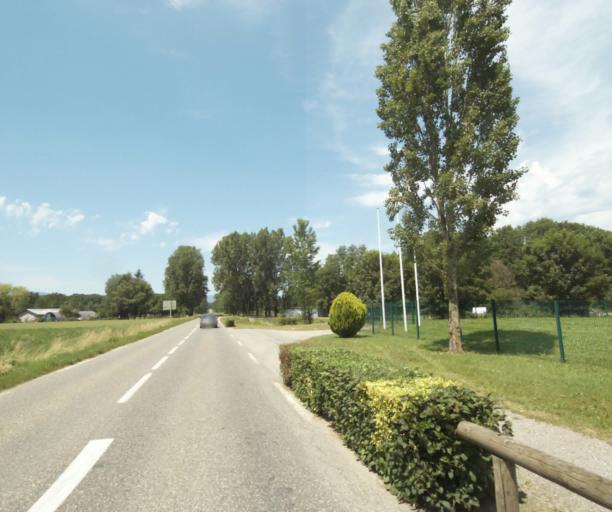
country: FR
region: Rhone-Alpes
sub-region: Departement de la Haute-Savoie
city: Douvaine
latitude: 46.3130
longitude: 6.3000
